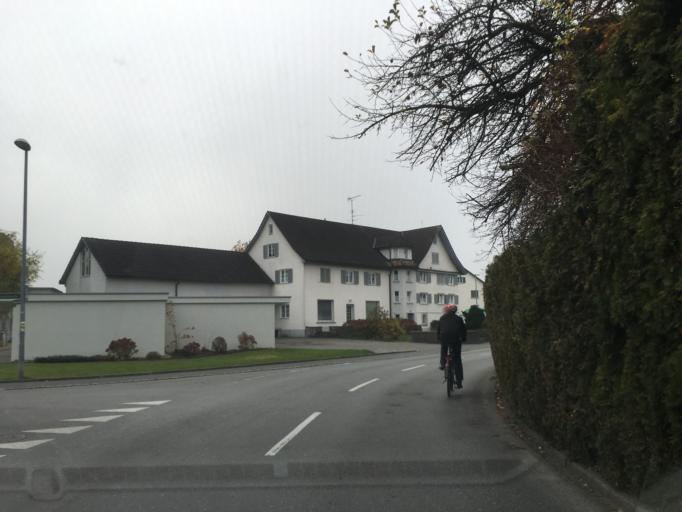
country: AT
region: Vorarlberg
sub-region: Politischer Bezirk Dornbirn
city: Lustenau
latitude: 47.4282
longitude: 9.6629
